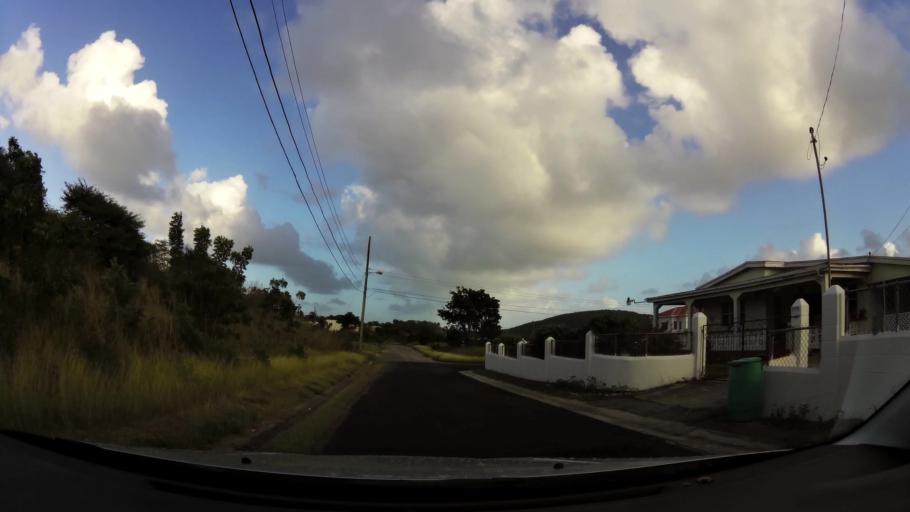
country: AG
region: Saint John
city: Saint John's
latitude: 17.1631
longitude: -61.8319
